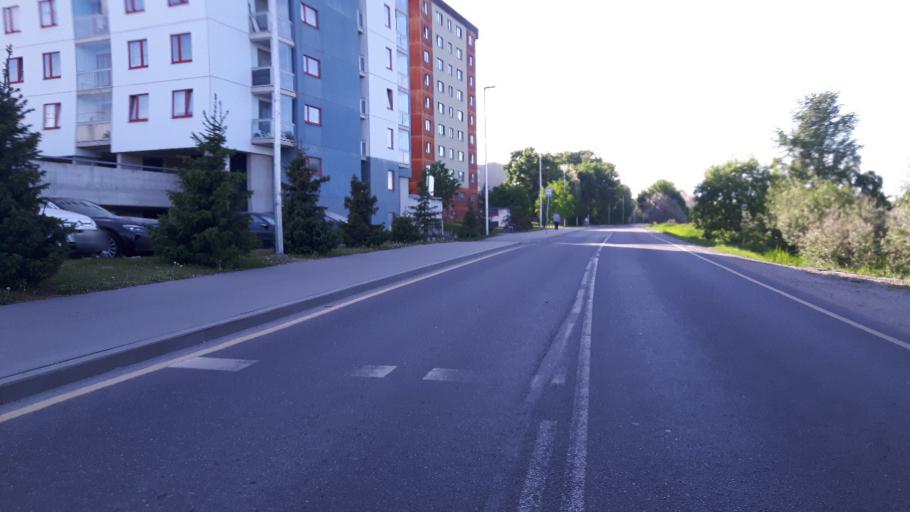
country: EE
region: Harju
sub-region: Tallinna linn
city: Kose
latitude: 59.4526
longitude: 24.8900
